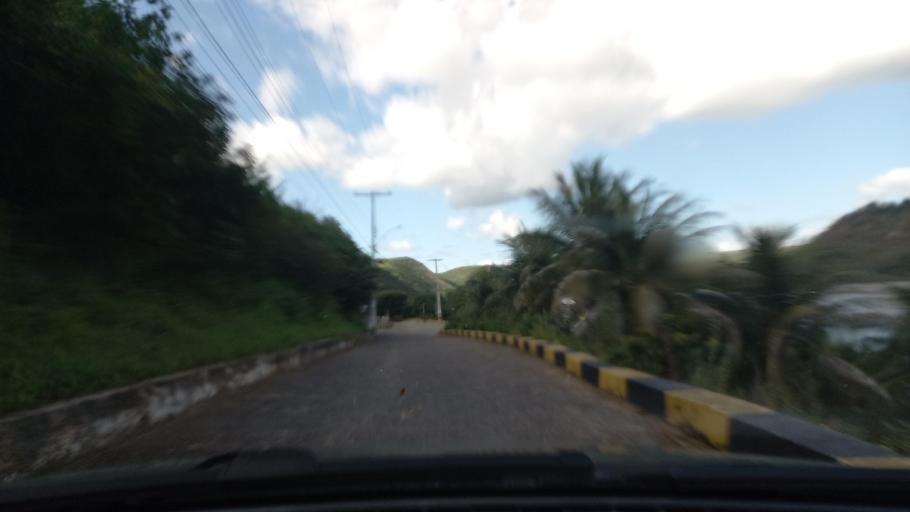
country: BR
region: Sergipe
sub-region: Caninde De Sao Francisco
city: Caninde de Sao Francisco
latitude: -9.6237
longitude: -37.7501
